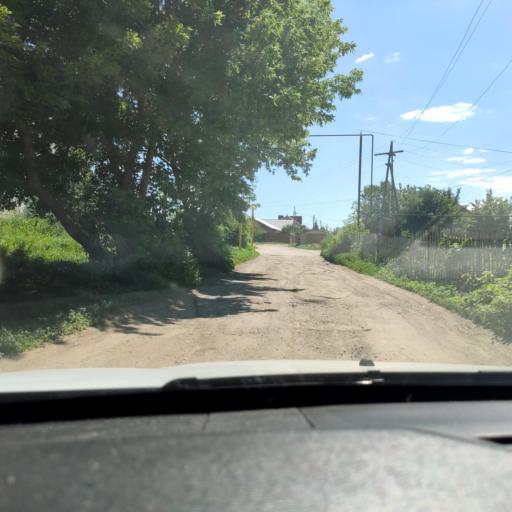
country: RU
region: Samara
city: Dubovyy Umet
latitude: 53.0358
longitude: 50.2486
